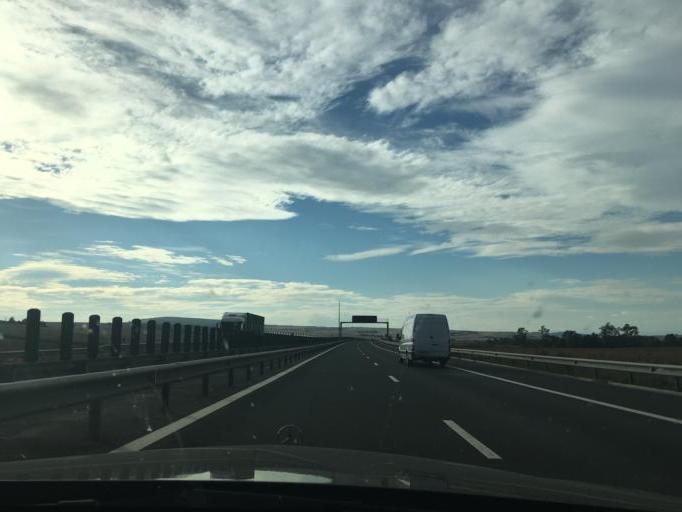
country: RO
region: Sibiu
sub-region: Oras Miercurea Sibiului
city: Miercurea Sibiului
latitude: 45.8989
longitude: 23.7734
